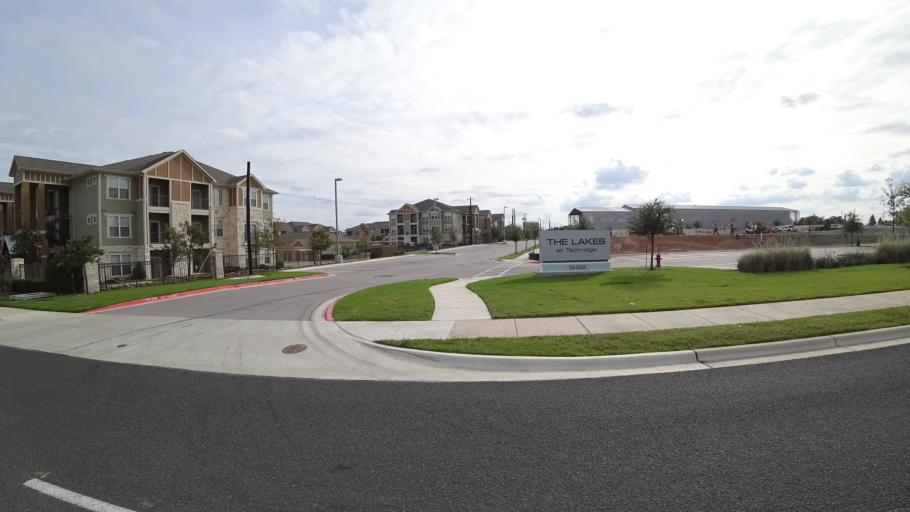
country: US
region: Texas
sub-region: Travis County
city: Wells Branch
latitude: 30.4297
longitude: -97.6669
